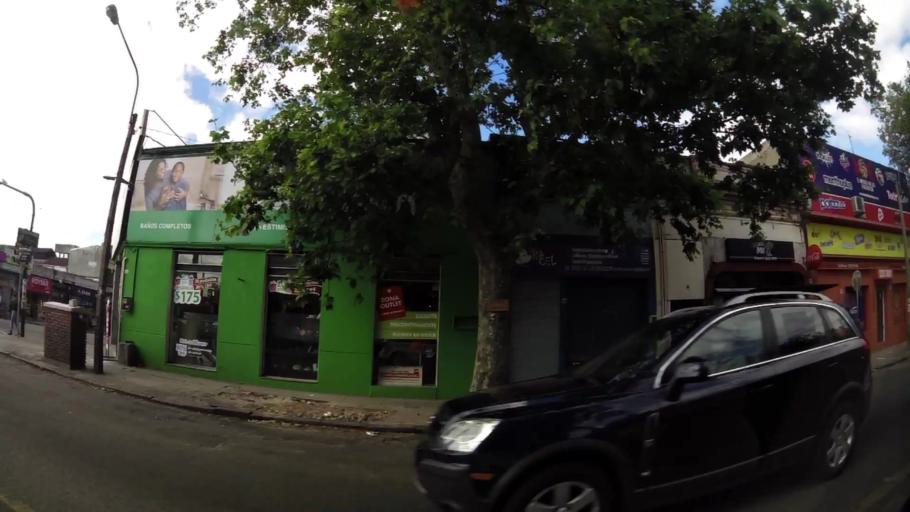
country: UY
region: Montevideo
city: Montevideo
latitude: -34.8763
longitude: -56.1798
